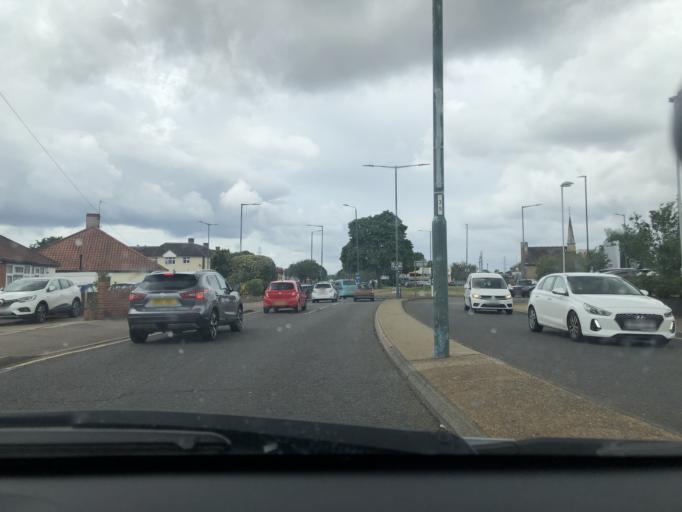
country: GB
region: England
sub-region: Greater London
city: Welling
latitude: 51.4480
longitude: 0.1200
